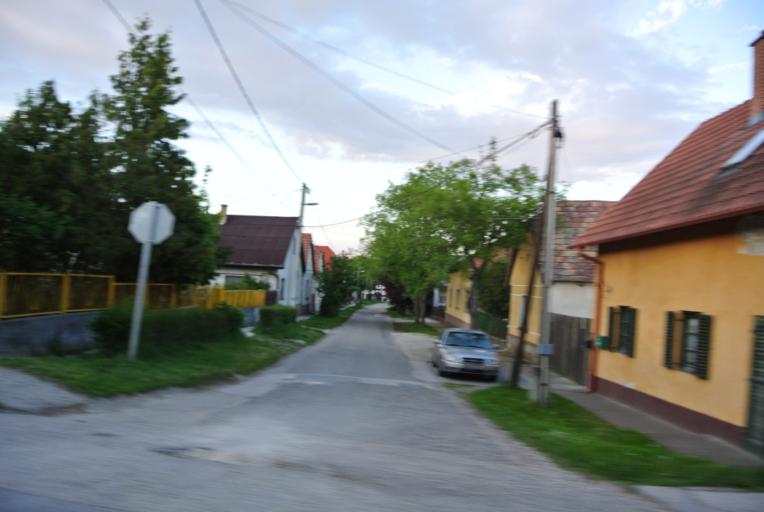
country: HU
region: Pest
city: Perbal
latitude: 47.5899
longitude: 18.7611
